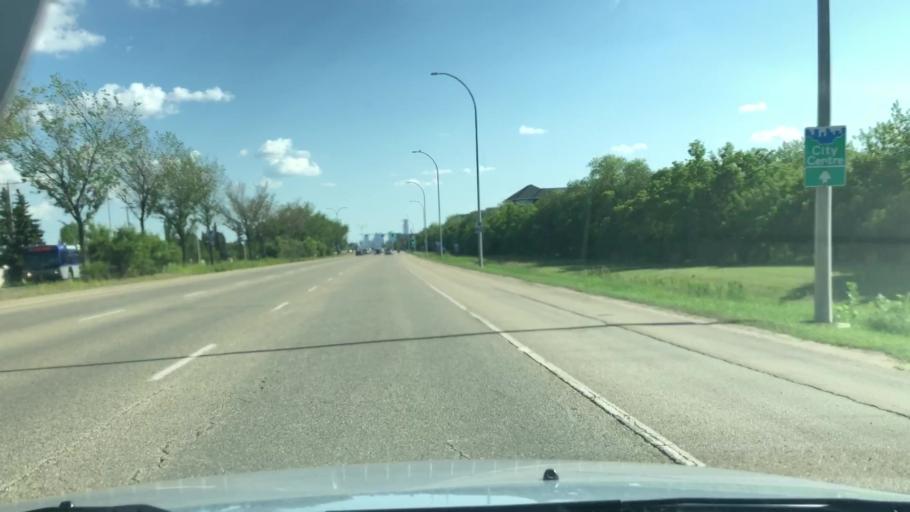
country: CA
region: Alberta
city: Edmonton
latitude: 53.6049
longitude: -113.4920
